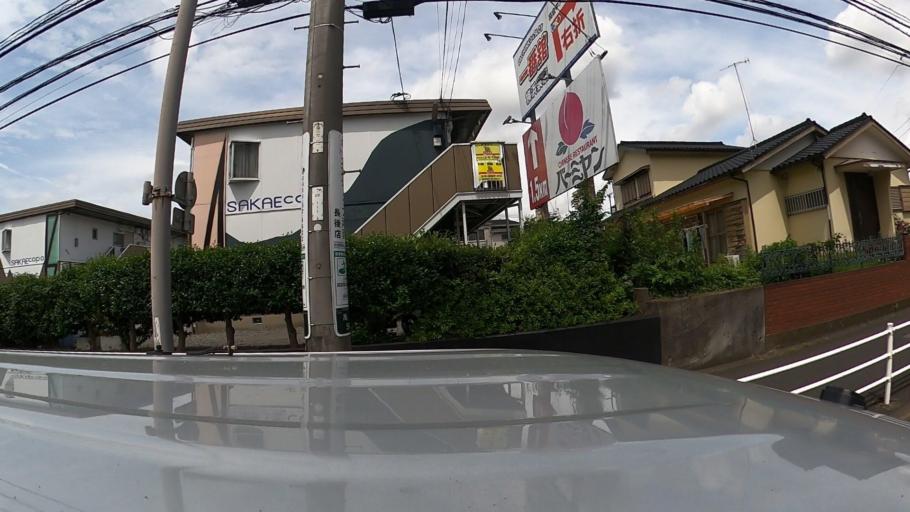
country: JP
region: Kanagawa
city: Fujisawa
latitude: 35.4059
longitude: 139.4698
